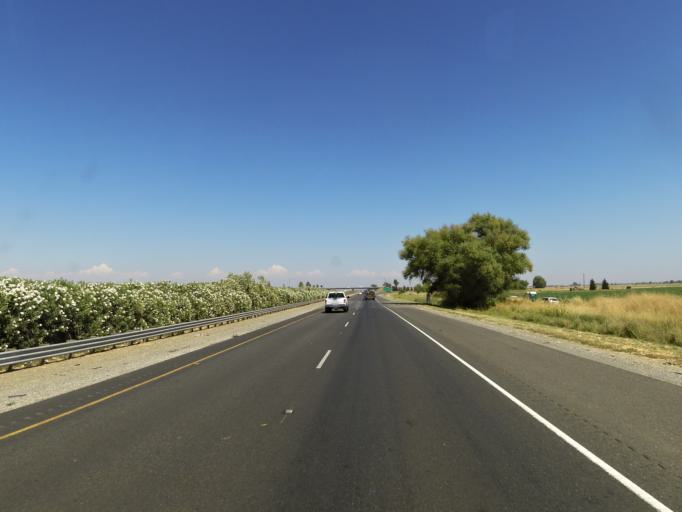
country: US
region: California
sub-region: Yolo County
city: West Sacramento
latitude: 38.6711
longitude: -121.5993
